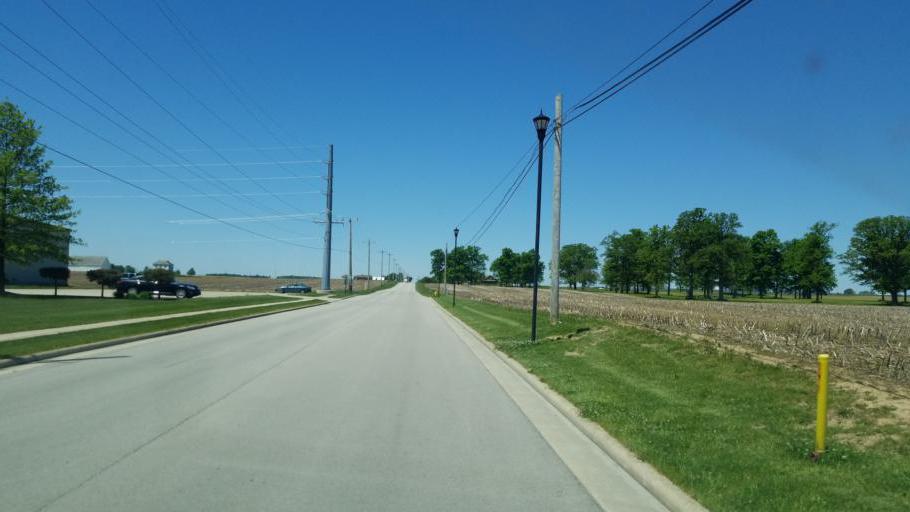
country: US
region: Ohio
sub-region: Auglaize County
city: Minster
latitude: 40.3856
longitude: -84.3897
